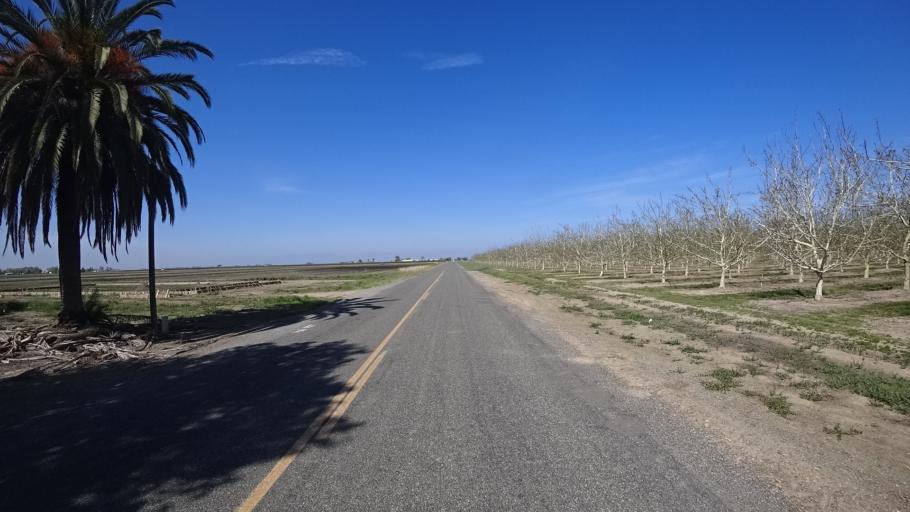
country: US
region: California
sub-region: Glenn County
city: Hamilton City
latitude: 39.6161
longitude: -122.0473
